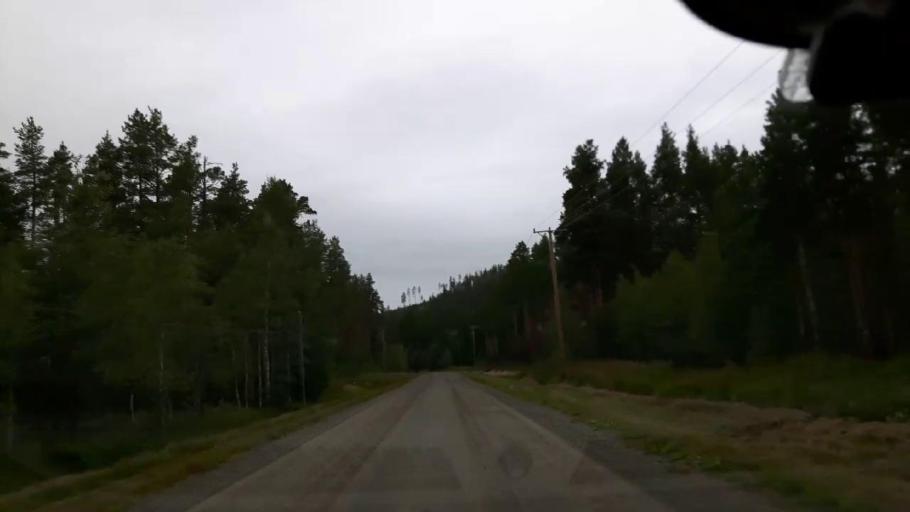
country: SE
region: Vaesternorrland
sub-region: Ange Kommun
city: Fransta
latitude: 62.7854
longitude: 16.0653
